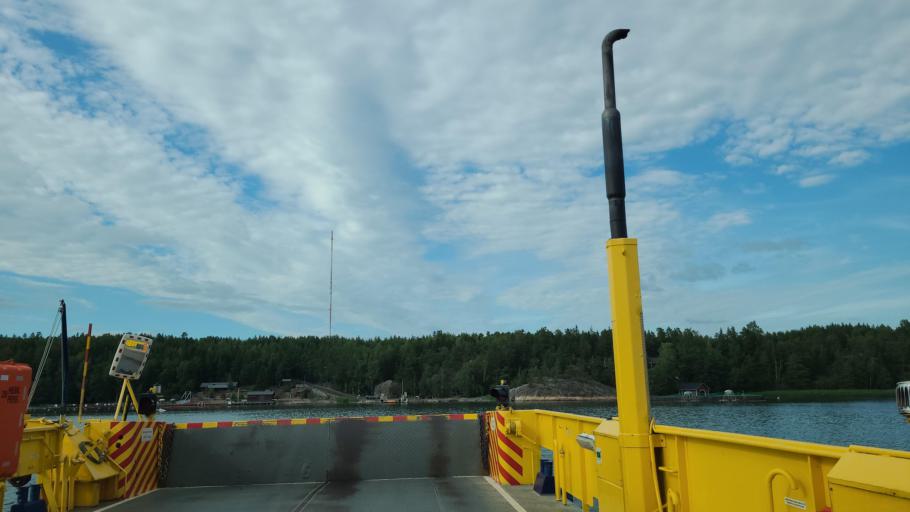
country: FI
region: Varsinais-Suomi
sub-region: Turku
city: Rymaettylae
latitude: 60.3140
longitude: 21.9617
